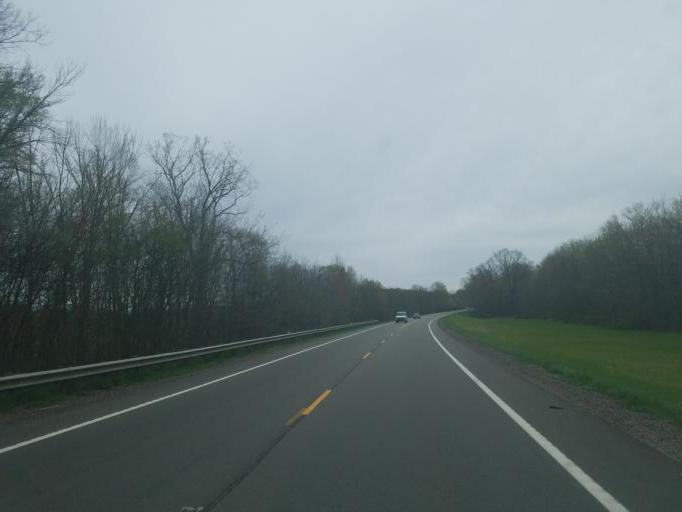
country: US
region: Ohio
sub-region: Wayne County
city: Doylestown
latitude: 40.9596
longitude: -81.7301
